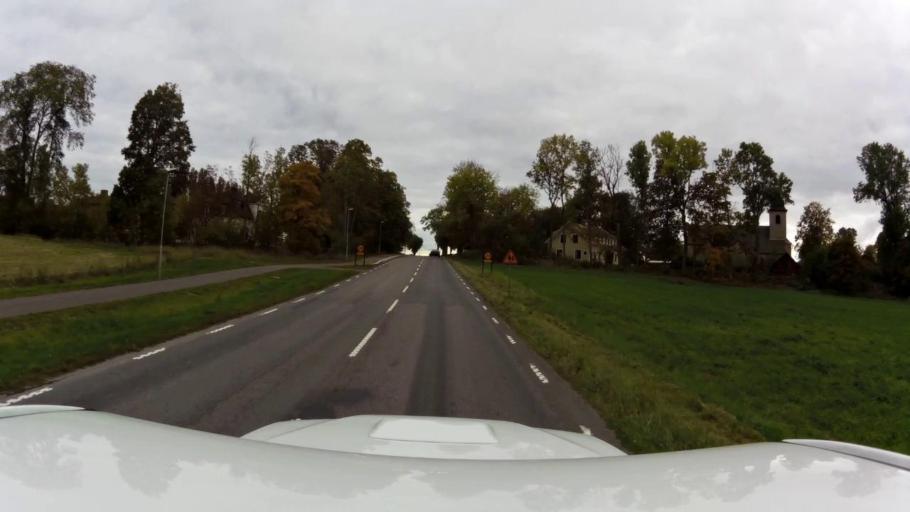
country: SE
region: OEstergoetland
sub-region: Linkopings Kommun
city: Berg
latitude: 58.4836
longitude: 15.5182
